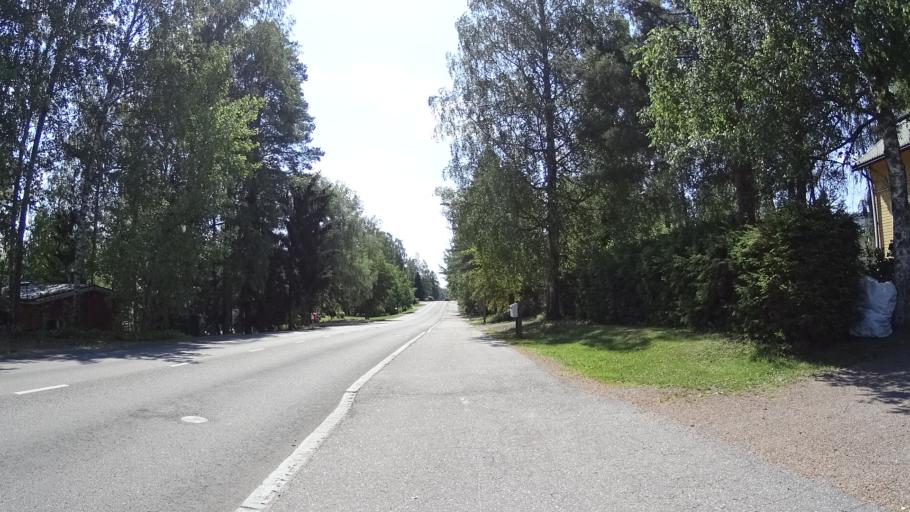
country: FI
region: Uusimaa
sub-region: Helsinki
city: Jaervenpaeae
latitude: 60.4840
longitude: 25.0671
